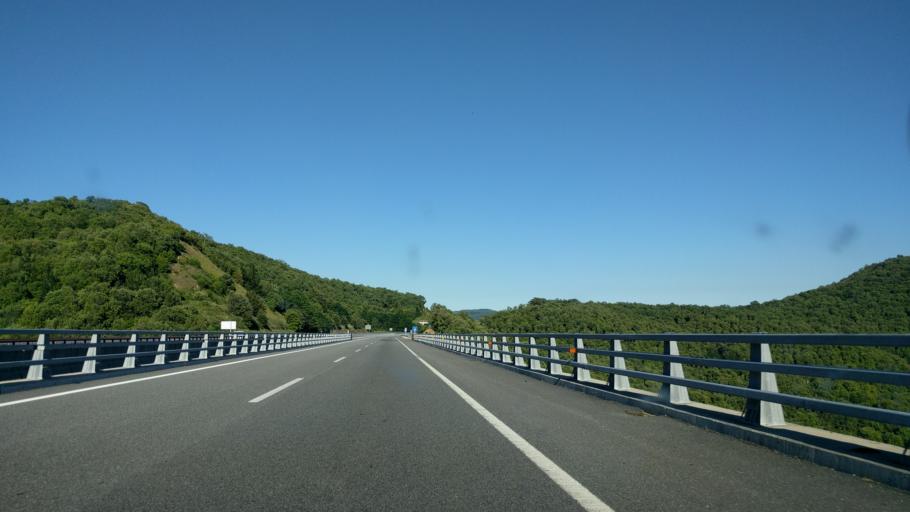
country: ES
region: Catalonia
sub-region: Provincia de Girona
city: Sant Hilari Sacalm
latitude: 41.8531
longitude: 2.4876
